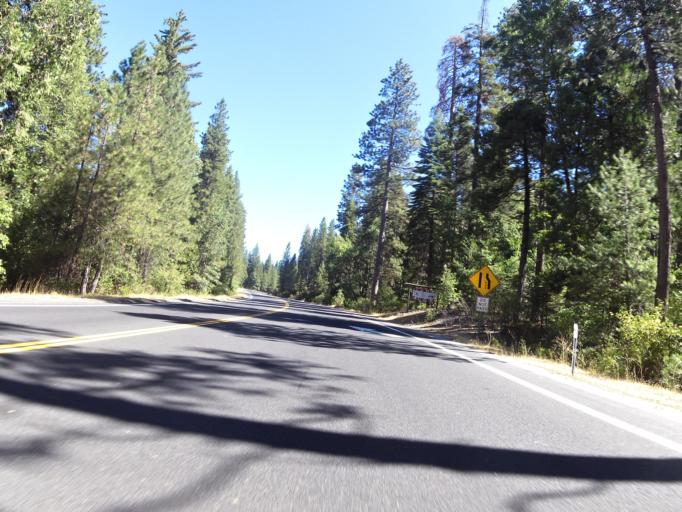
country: US
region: California
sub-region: Calaveras County
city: Arnold
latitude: 38.2615
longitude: -120.3378
